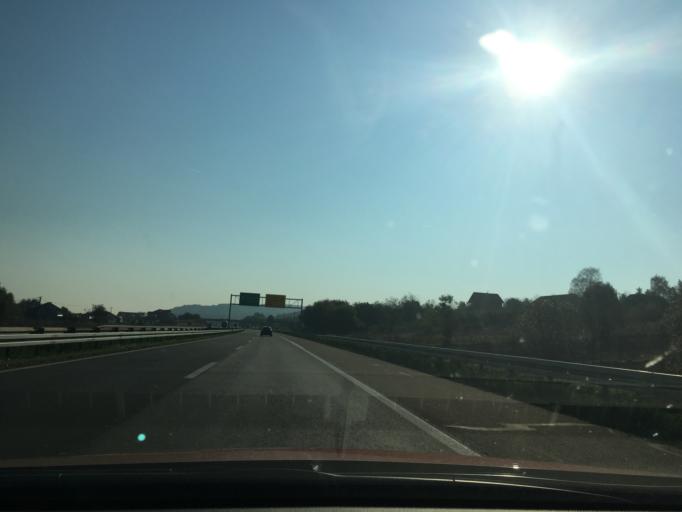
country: RS
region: Central Serbia
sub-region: Belgrade
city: Grocka
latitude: 44.5754
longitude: 20.7411
